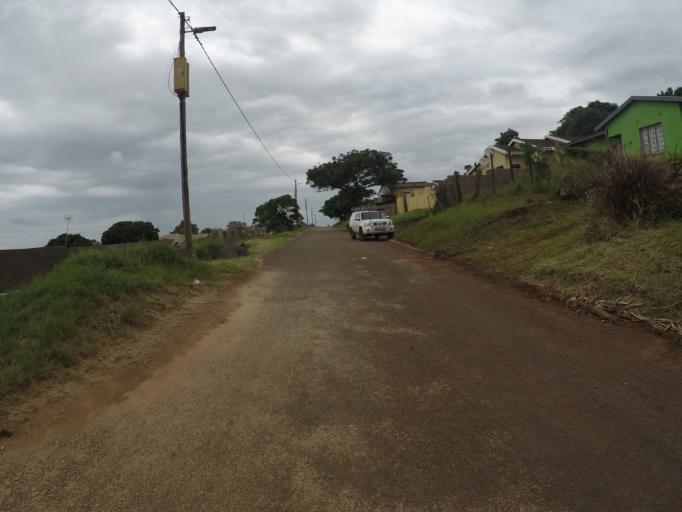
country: ZA
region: KwaZulu-Natal
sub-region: uThungulu District Municipality
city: Empangeni
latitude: -28.7762
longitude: 31.8634
